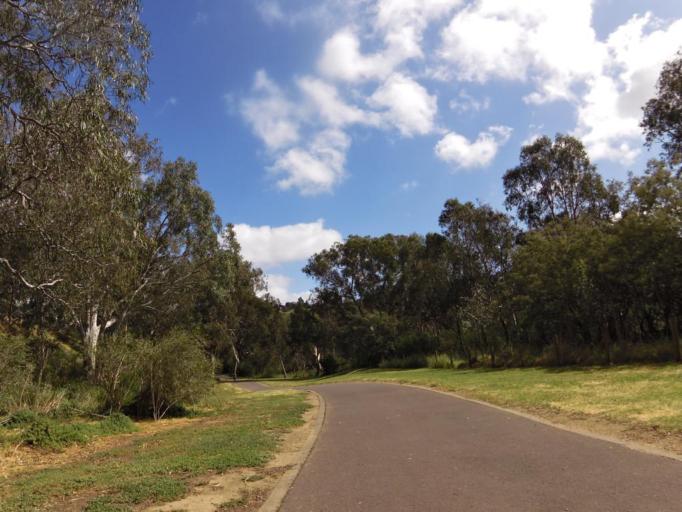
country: AU
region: Victoria
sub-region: Brimbank
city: Keilor
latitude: -37.7263
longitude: 144.8340
